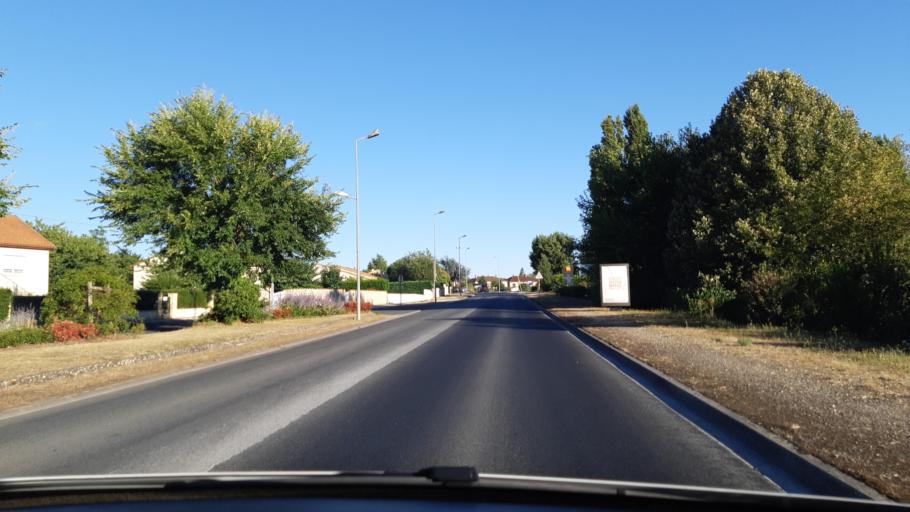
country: FR
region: Poitou-Charentes
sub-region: Departement des Deux-Sevres
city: Exireuil
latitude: 46.4190
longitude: -0.2048
